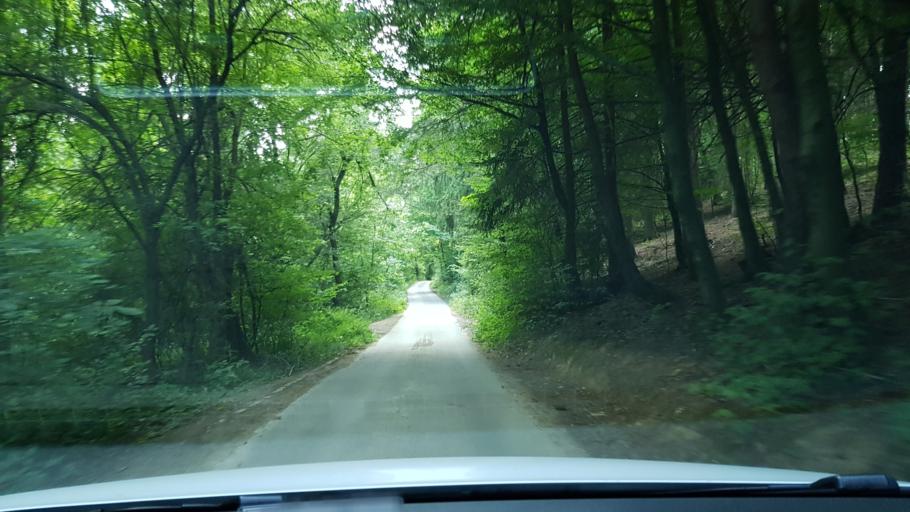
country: SK
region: Trenciansky
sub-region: Okres Povazska Bystrica
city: Povazska Bystrica
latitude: 49.1116
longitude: 18.4618
